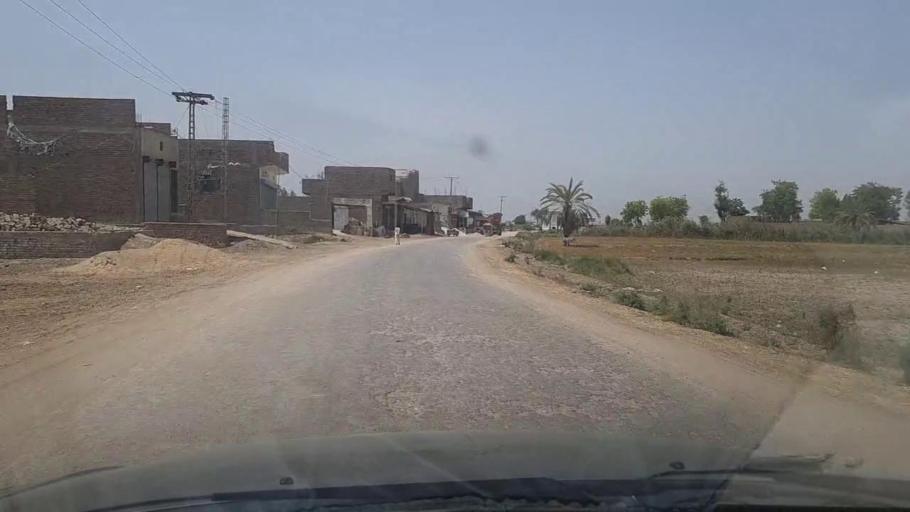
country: PK
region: Sindh
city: Bhiria
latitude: 26.8861
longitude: 68.2689
